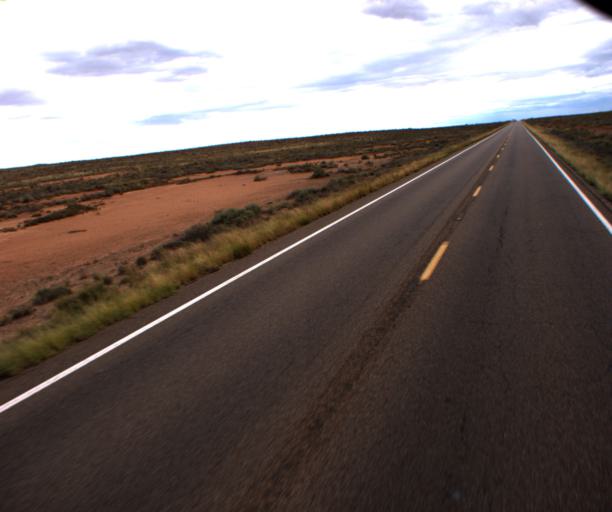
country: US
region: Arizona
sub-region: Navajo County
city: Holbrook
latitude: 34.8217
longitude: -110.1411
